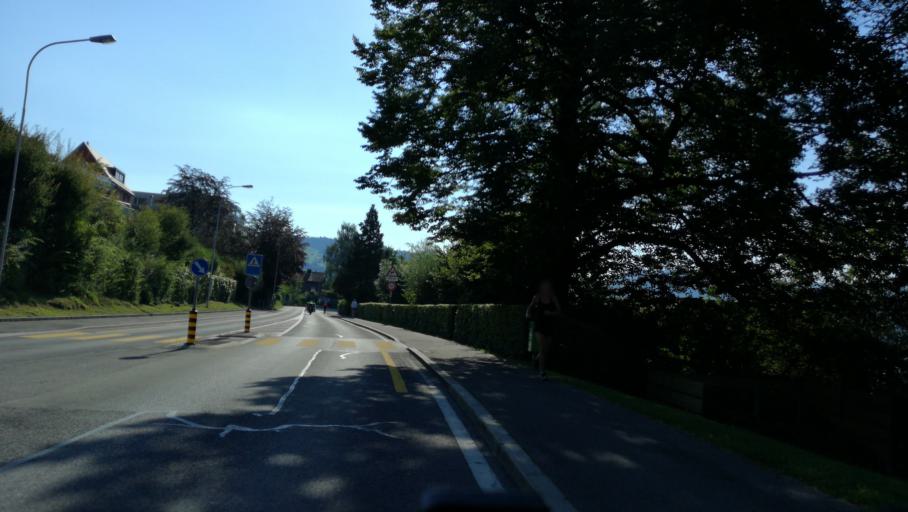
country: CH
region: Zug
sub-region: Zug
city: Unterageri
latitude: 47.1374
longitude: 8.5940
